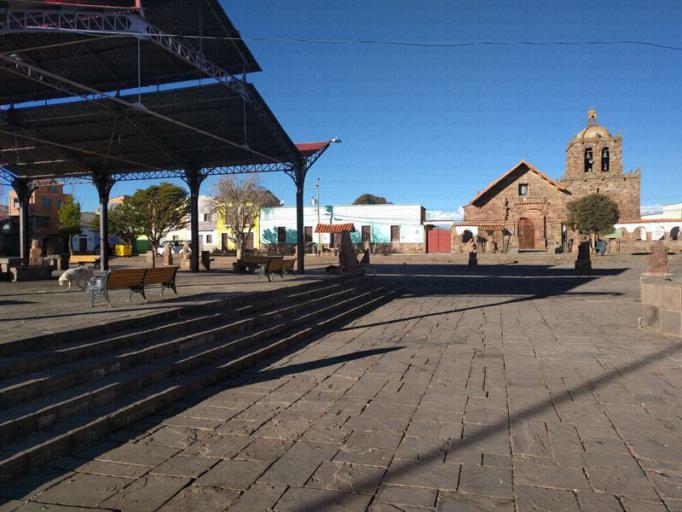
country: BO
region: La Paz
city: Tiahuanaco
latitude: -16.5528
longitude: -68.6816
